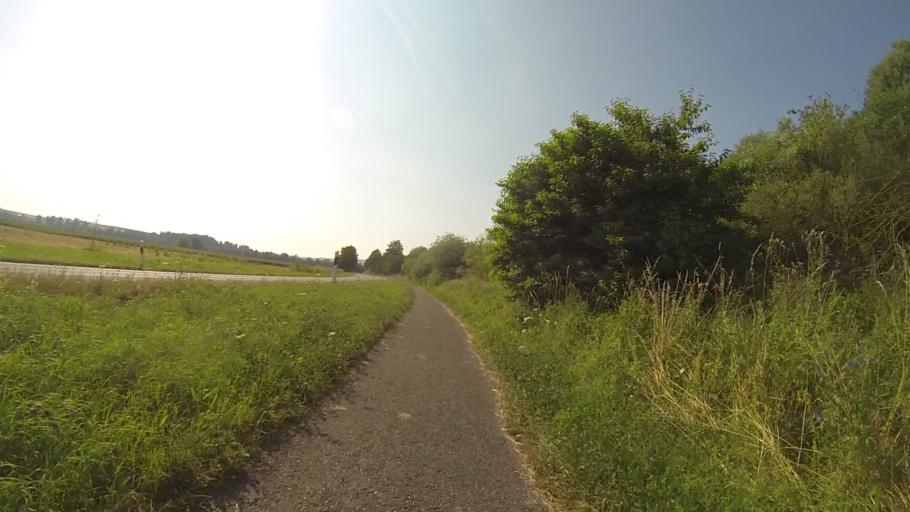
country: DE
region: Baden-Wuerttemberg
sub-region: Tuebingen Region
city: Erbach
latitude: 48.3485
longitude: 9.9333
